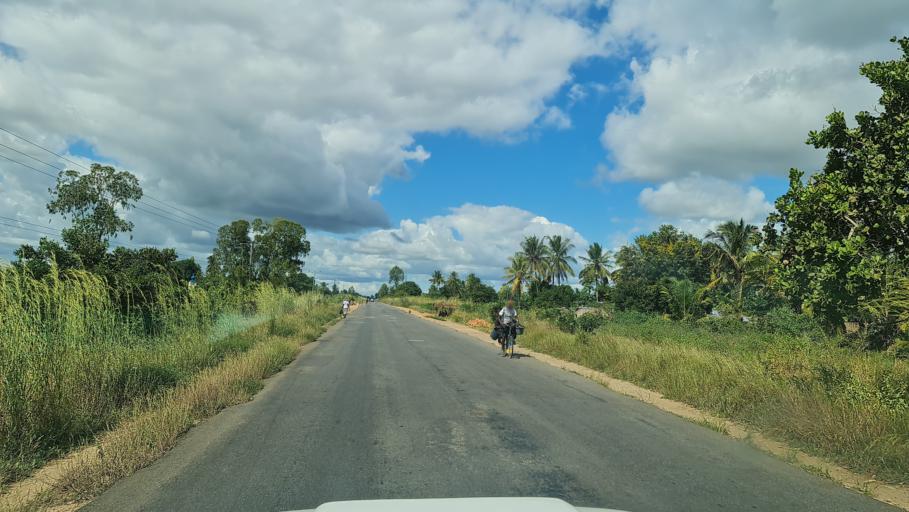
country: MZ
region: Zambezia
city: Quelimane
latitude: -17.5886
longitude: 36.7578
